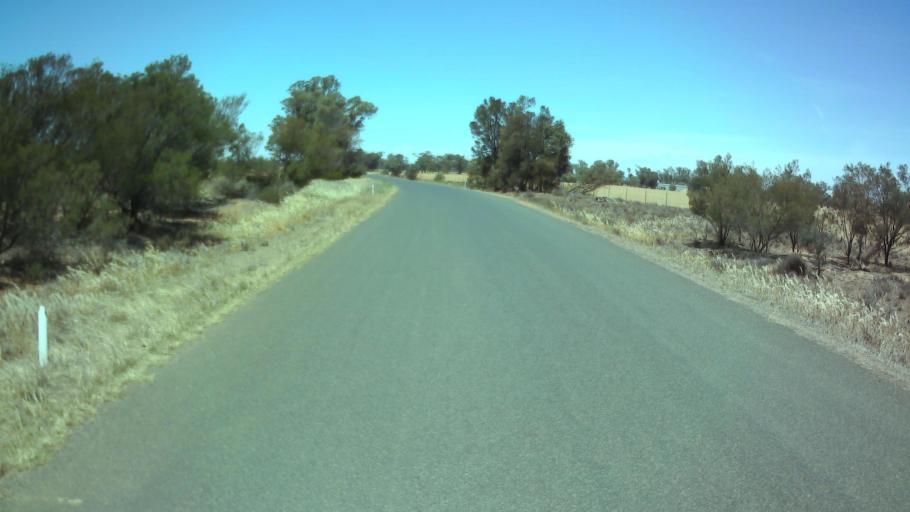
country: AU
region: New South Wales
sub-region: Weddin
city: Grenfell
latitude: -34.0585
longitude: 147.7797
